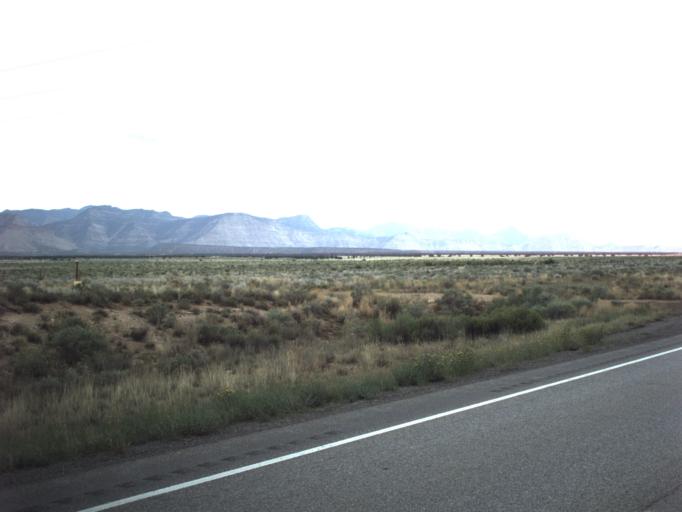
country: US
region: Utah
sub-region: Carbon County
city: East Carbon City
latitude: 39.4465
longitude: -110.4706
